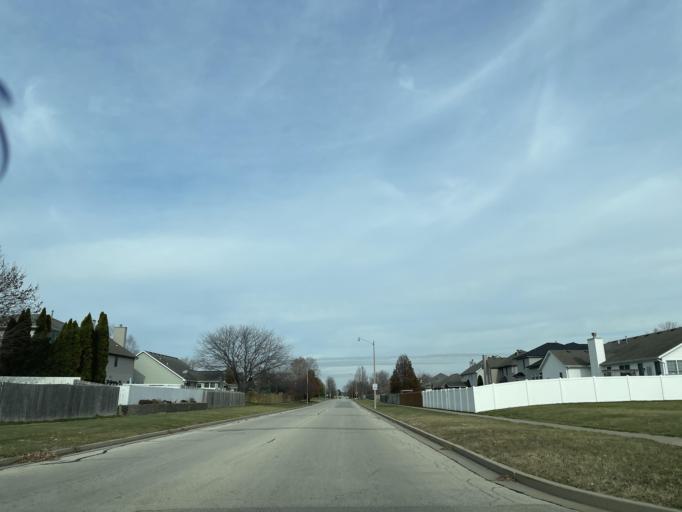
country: US
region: Illinois
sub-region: Sangamon County
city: Jerome
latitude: 39.7641
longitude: -89.7297
